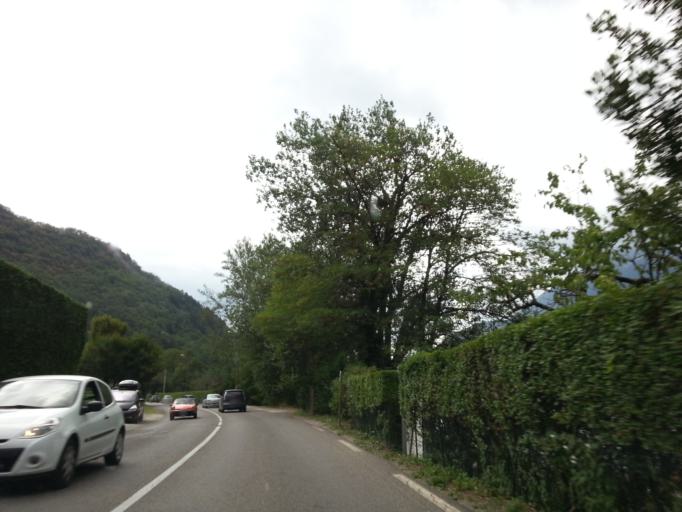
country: FR
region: Rhone-Alpes
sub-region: Departement de la Haute-Savoie
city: Talloires
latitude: 45.8172
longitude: 6.2080
